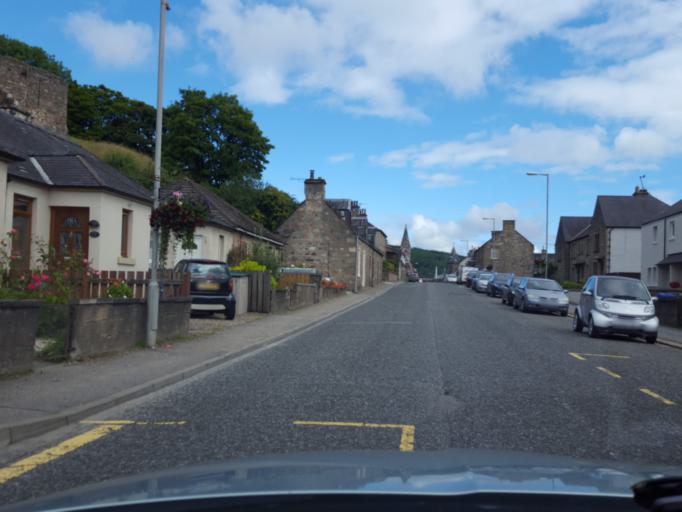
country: GB
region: Scotland
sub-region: Moray
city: Rothes
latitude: 57.5243
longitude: -3.2084
